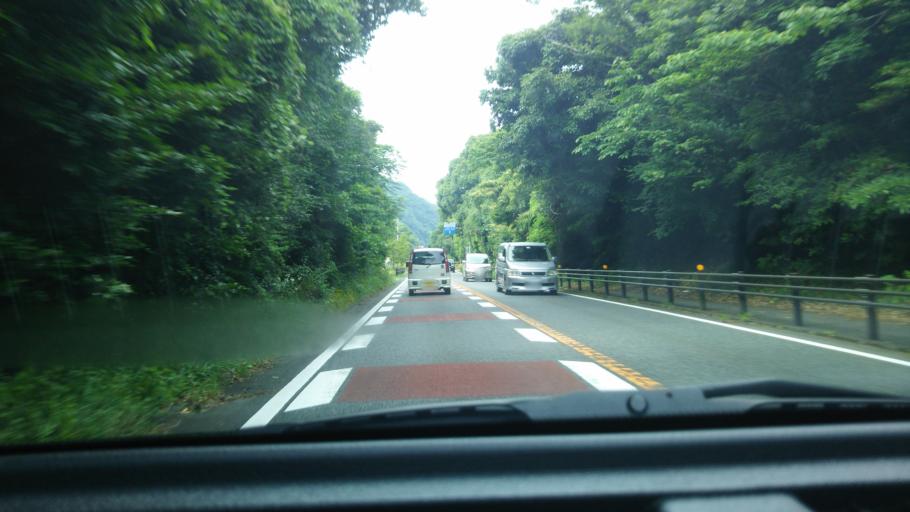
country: JP
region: Shizuoka
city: Ito
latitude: 34.8644
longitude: 139.0954
